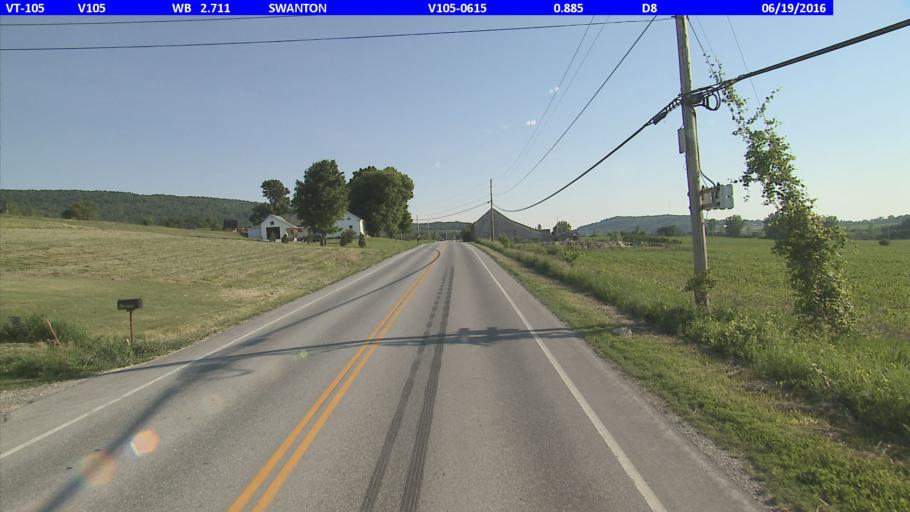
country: US
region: Vermont
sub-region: Franklin County
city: Saint Albans
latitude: 44.8462
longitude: -73.0400
